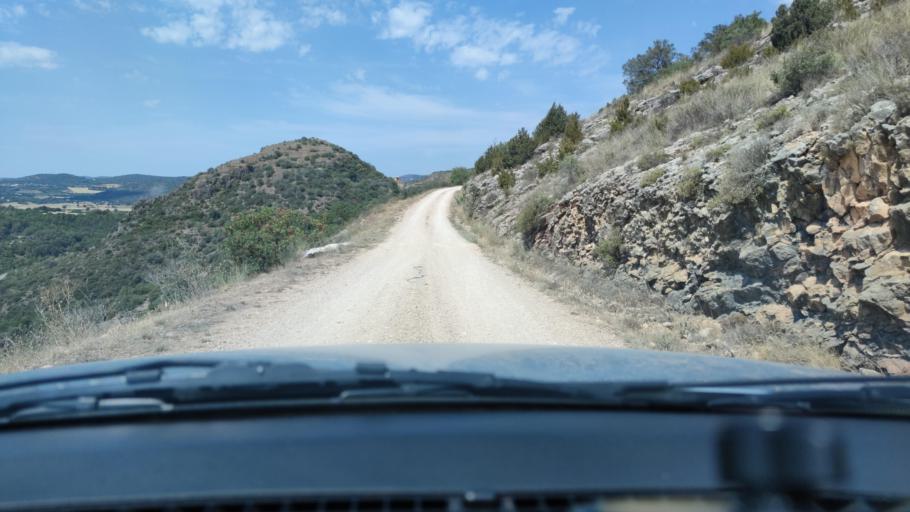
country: ES
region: Catalonia
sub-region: Provincia de Lleida
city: Ager
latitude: 41.9277
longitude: 0.8098
